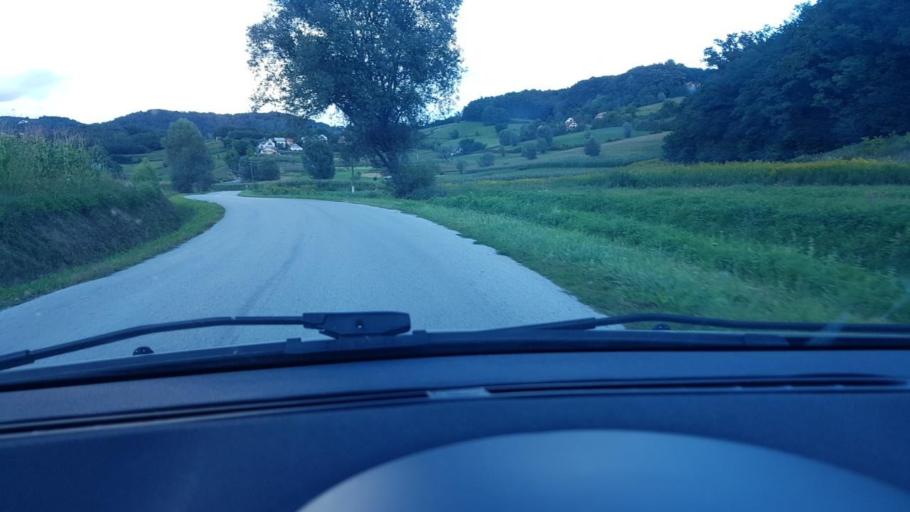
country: HR
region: Krapinsko-Zagorska
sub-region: Grad Krapina
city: Krapina
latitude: 46.1531
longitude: 15.8247
